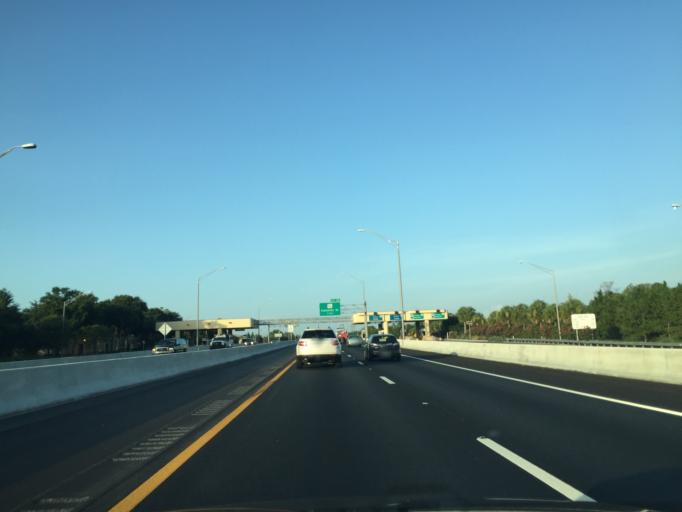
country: US
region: Florida
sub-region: Orange County
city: Union Park
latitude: 28.5889
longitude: -81.2544
